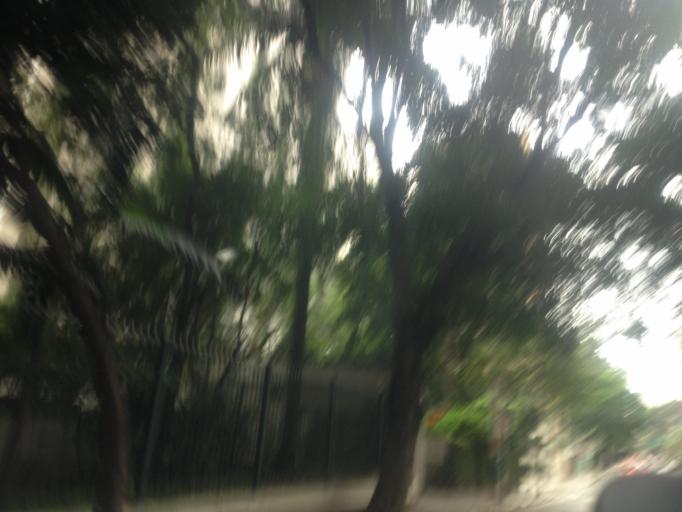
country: BR
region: Sao Paulo
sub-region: Sao Paulo
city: Sao Paulo
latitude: -23.6134
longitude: -46.6803
